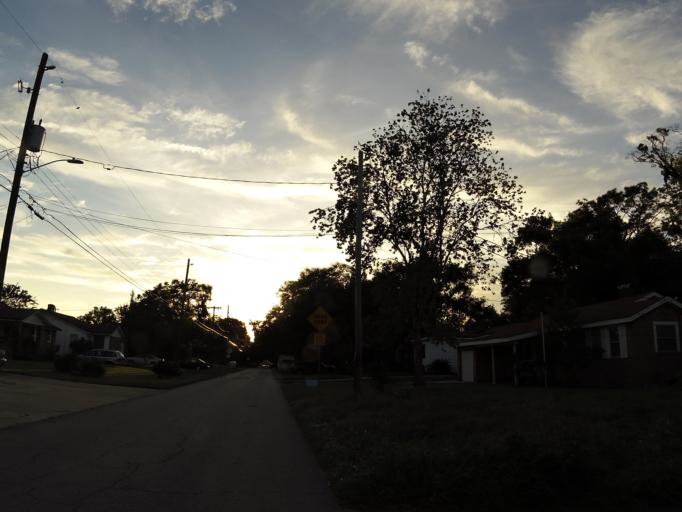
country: US
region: Florida
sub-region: Duval County
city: Jacksonville
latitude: 30.2772
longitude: -81.7247
